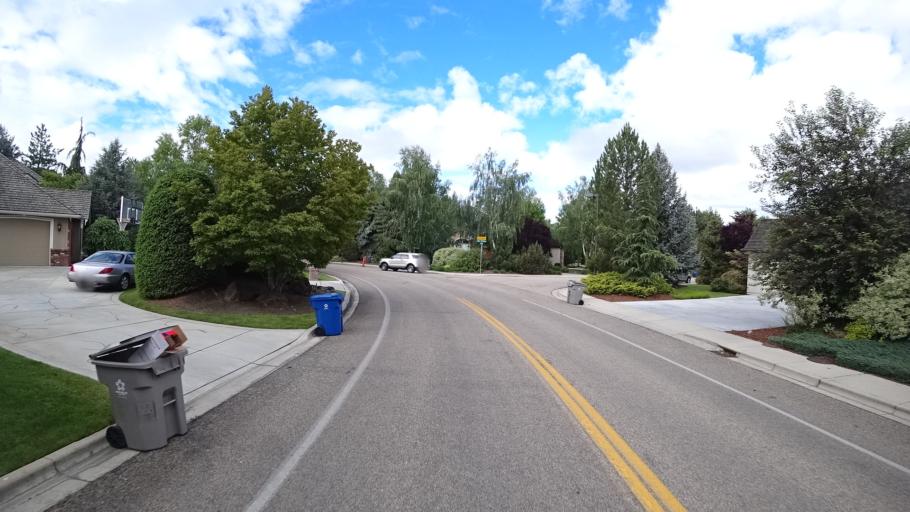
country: US
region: Idaho
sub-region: Ada County
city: Eagle
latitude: 43.6705
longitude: -116.2975
